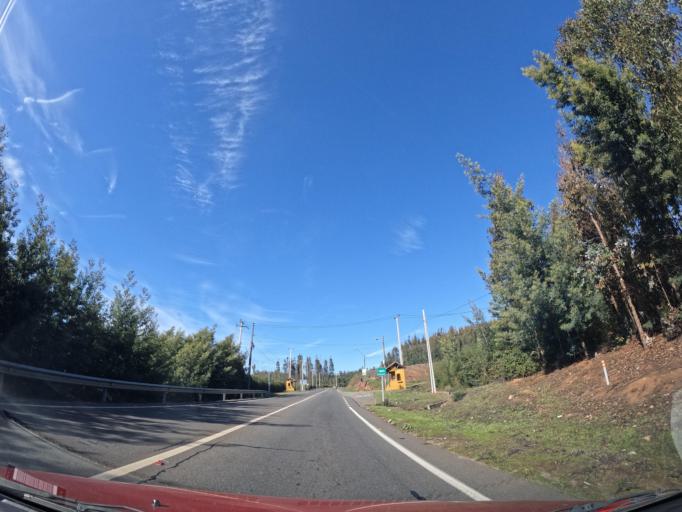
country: CL
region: Biobio
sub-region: Provincia de Concepcion
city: Penco
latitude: -36.8254
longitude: -72.7275
